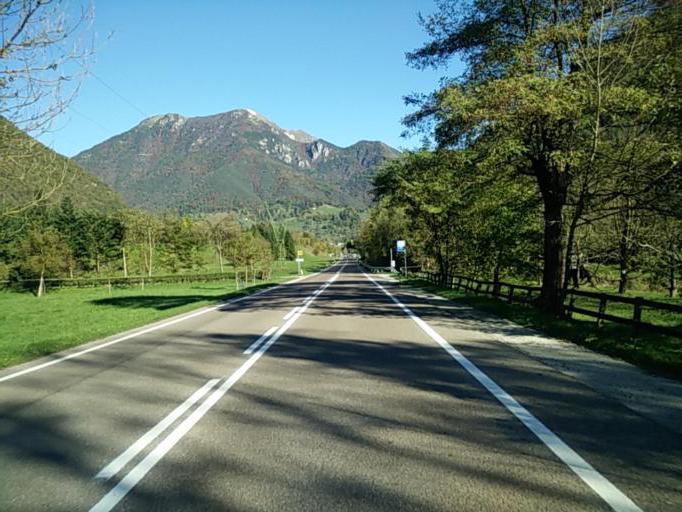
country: IT
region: Trentino-Alto Adige
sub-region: Provincia di Trento
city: Pieve di Ledro
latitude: 45.8928
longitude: 10.7020
